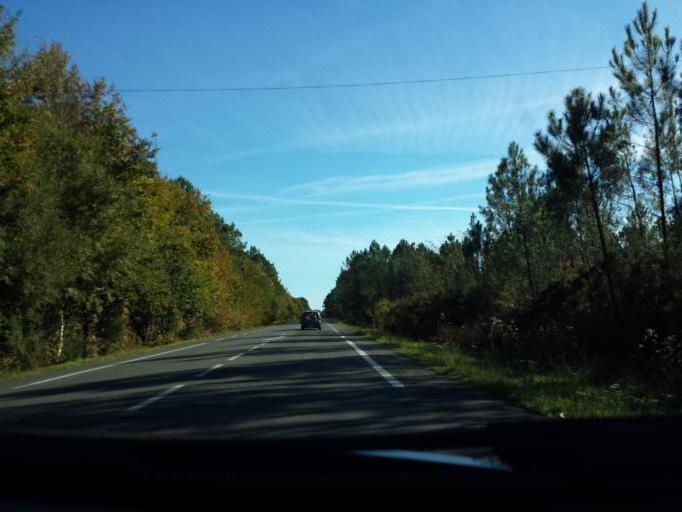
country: FR
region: Aquitaine
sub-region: Departement de la Gironde
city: Lacanau
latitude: 44.9761
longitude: -1.0427
